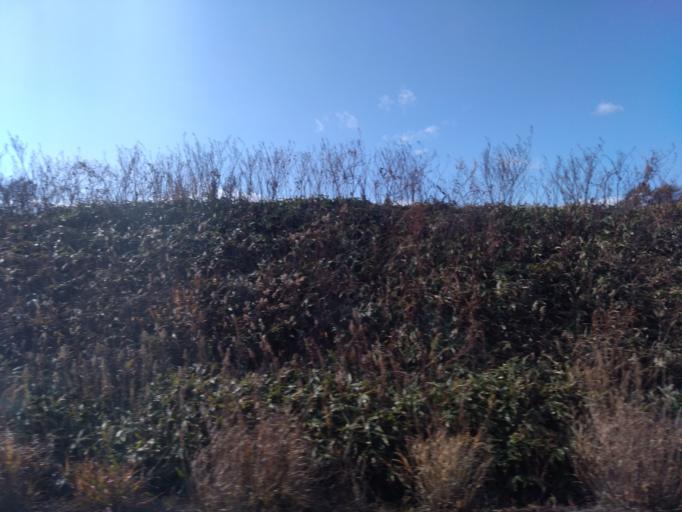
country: JP
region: Hokkaido
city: Kitahiroshima
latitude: 42.9344
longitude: 141.5724
